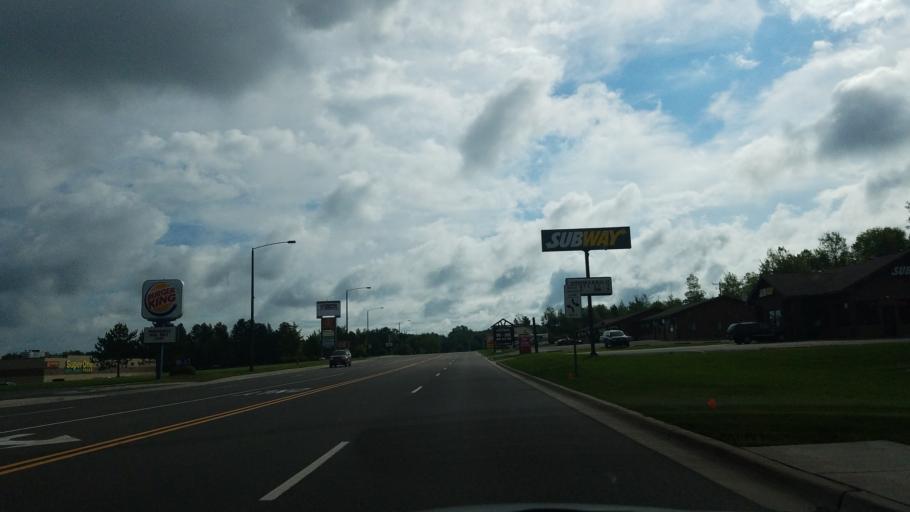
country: US
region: Michigan
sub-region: Gogebic County
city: Ironwood
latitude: 46.4632
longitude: -90.1453
